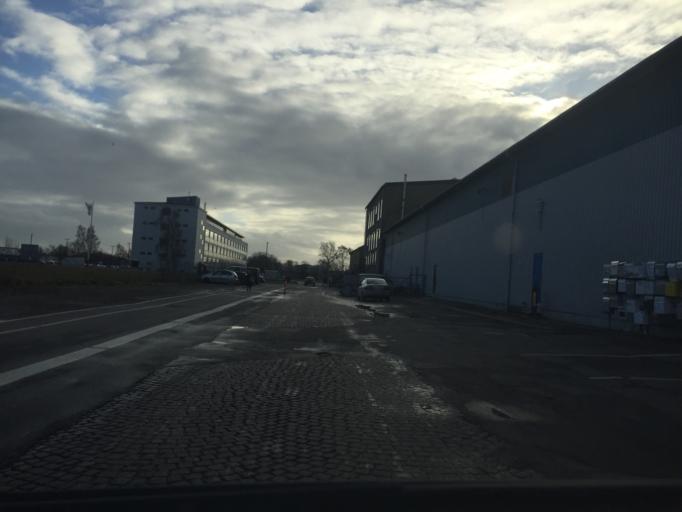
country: DK
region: Capital Region
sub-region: Kobenhavn
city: Christianshavn
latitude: 55.6912
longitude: 12.6119
